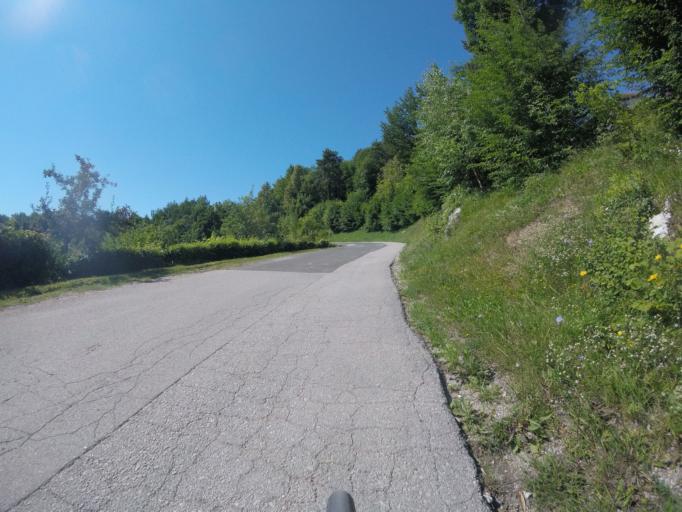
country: SI
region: Brezice
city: Brezice
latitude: 45.8378
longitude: 15.5680
